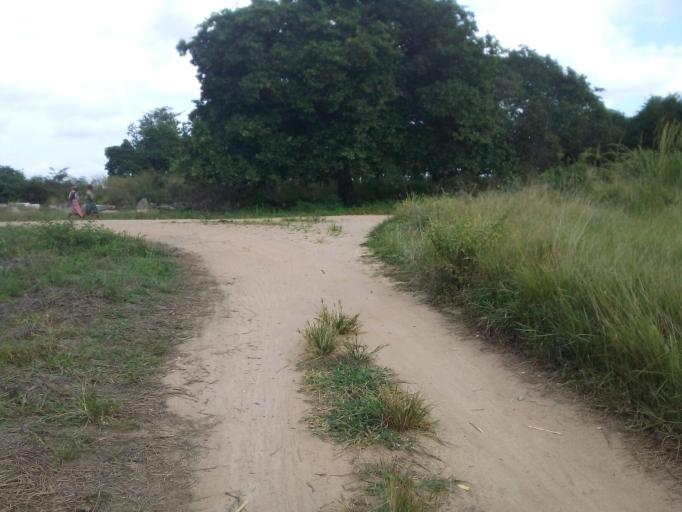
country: MZ
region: Zambezia
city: Quelimane
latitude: -17.5545
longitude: 36.6985
